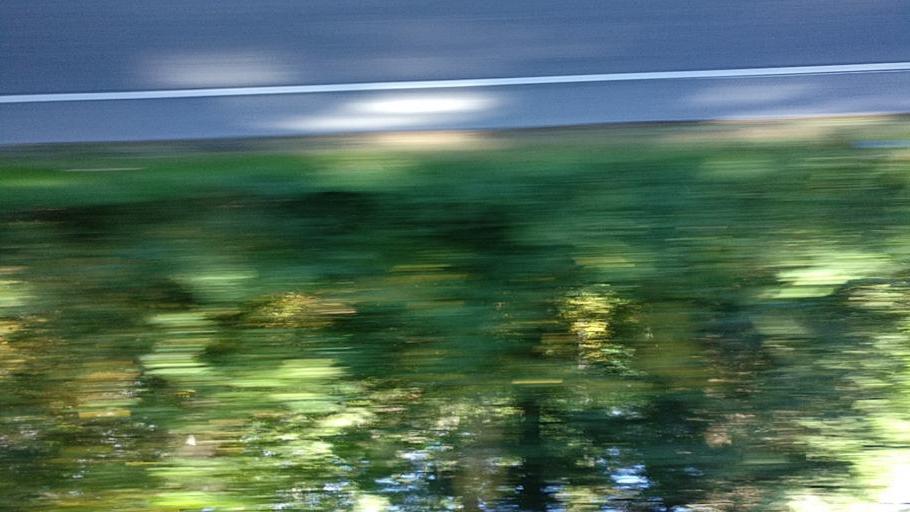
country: CA
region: British Columbia
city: Surrey
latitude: 49.0649
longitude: -122.8394
